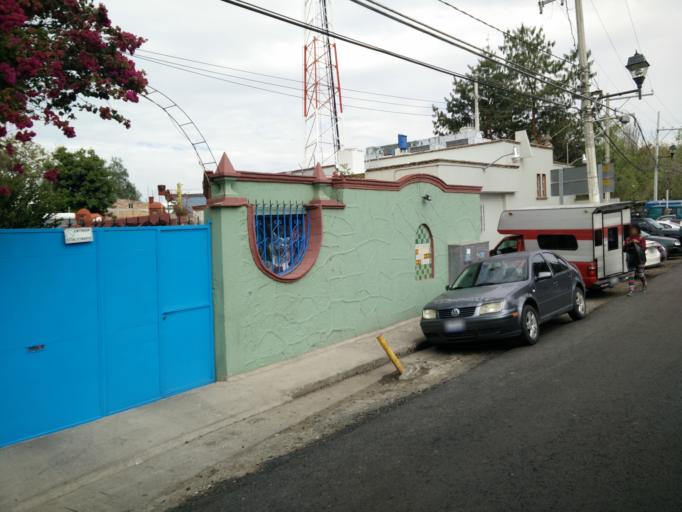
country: MX
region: Queretaro
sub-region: Tequisquiapan
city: Tequisquiapan
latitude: 20.5223
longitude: -99.8899
